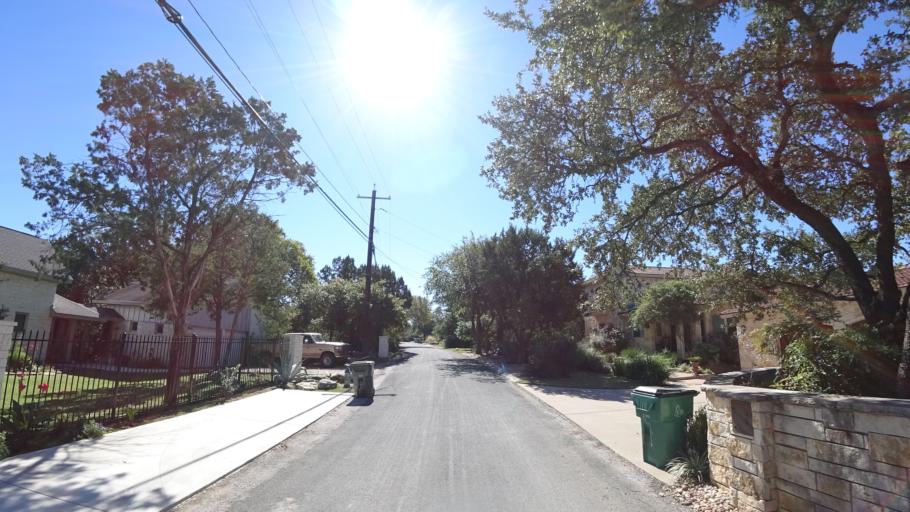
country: US
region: Texas
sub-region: Travis County
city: West Lake Hills
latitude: 30.3180
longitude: -97.8056
